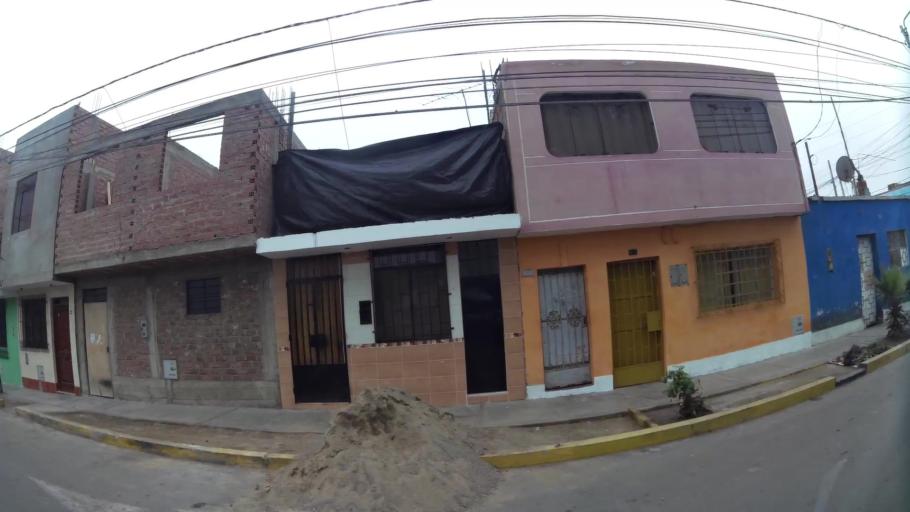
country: PE
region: Ica
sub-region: Provincia de Pisco
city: Pisco
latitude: -13.7138
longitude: -76.1992
